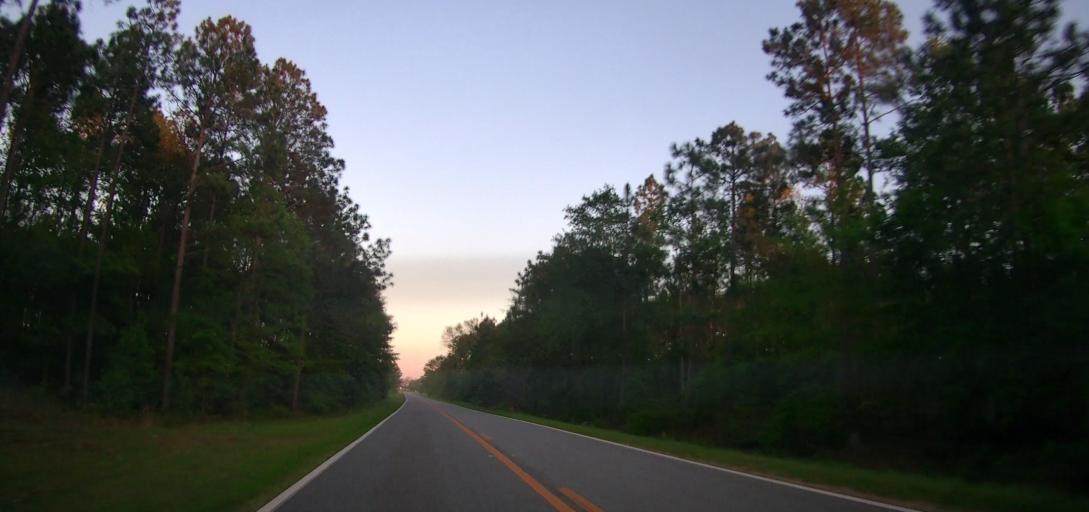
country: US
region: Georgia
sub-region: Wilcox County
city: Rochelle
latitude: 31.7946
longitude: -83.4433
